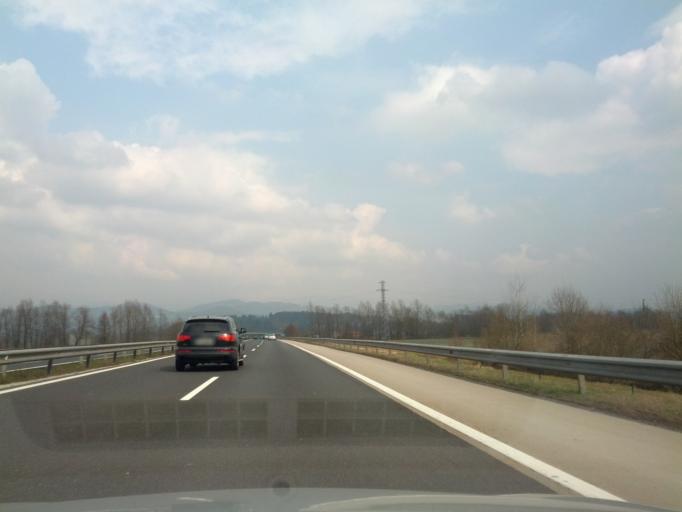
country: SI
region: Domzale
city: Dob
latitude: 46.1438
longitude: 14.6339
